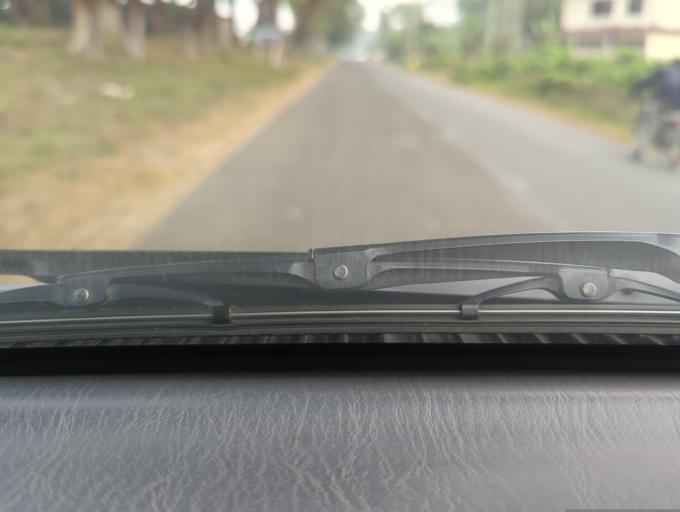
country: BD
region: Sylhet
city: Maulavi Bazar
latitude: 24.5091
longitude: 91.7289
